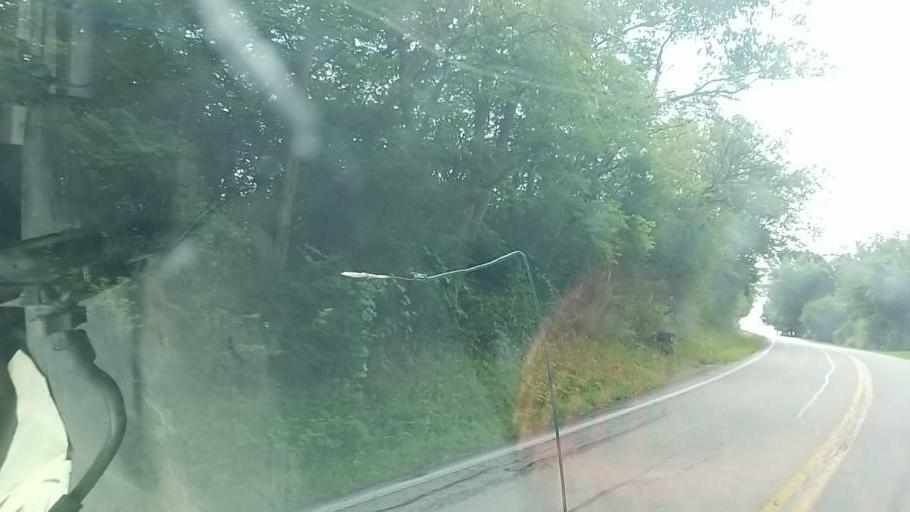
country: US
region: Ohio
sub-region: Pickaway County
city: Commercial Point
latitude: 39.7918
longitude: -83.1700
